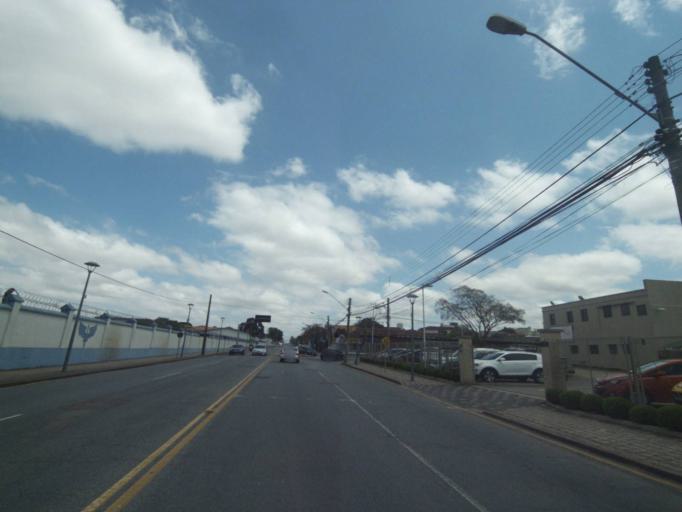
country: BR
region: Parana
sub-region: Curitiba
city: Curitiba
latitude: -25.3981
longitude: -49.2350
